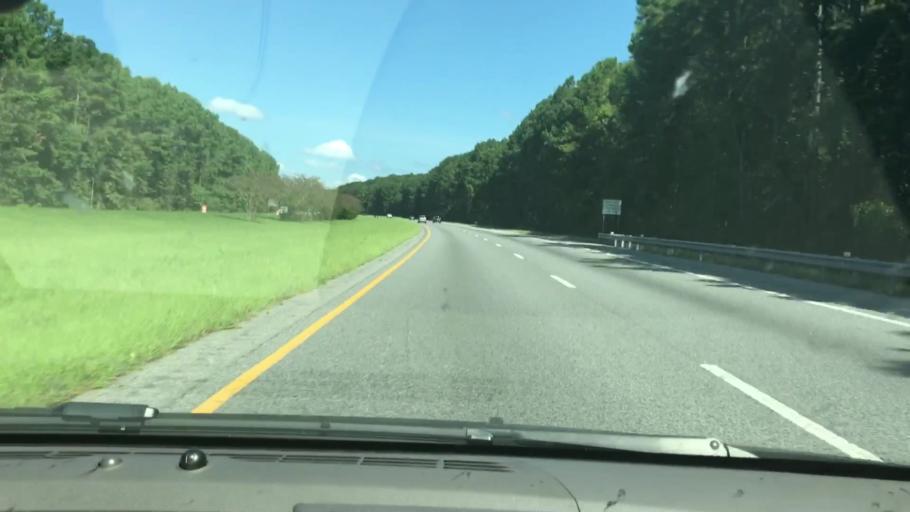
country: US
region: Alabama
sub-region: Russell County
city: Phenix City
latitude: 32.6207
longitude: -84.9526
